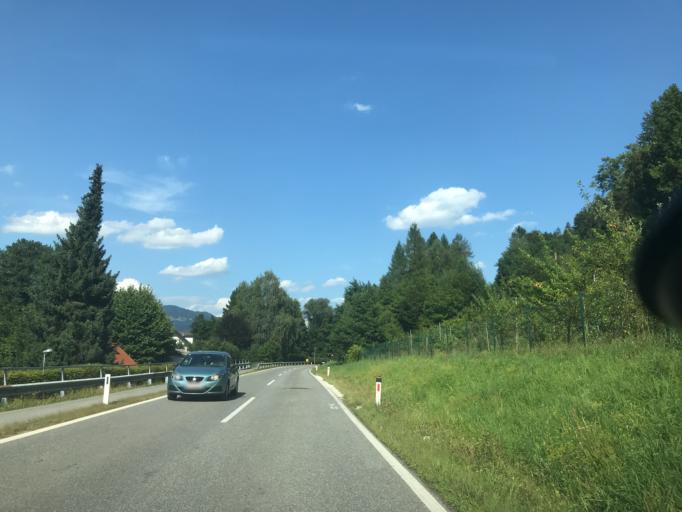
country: AT
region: Carinthia
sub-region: Politischer Bezirk Feldkirchen
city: Ossiach
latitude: 46.6588
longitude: 13.9499
